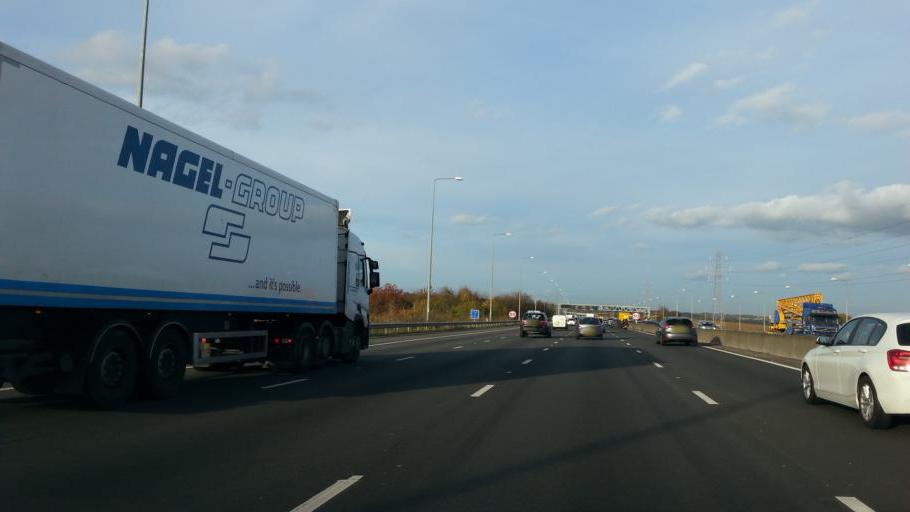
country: GB
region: England
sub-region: Buckinghamshire
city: Chalfont Saint Peter
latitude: 51.6020
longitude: -0.5300
